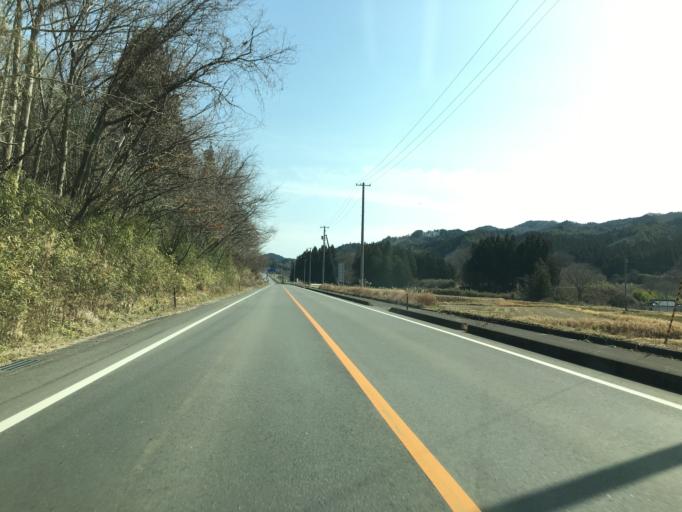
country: JP
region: Ibaraki
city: Daigo
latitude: 36.8192
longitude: 140.4603
